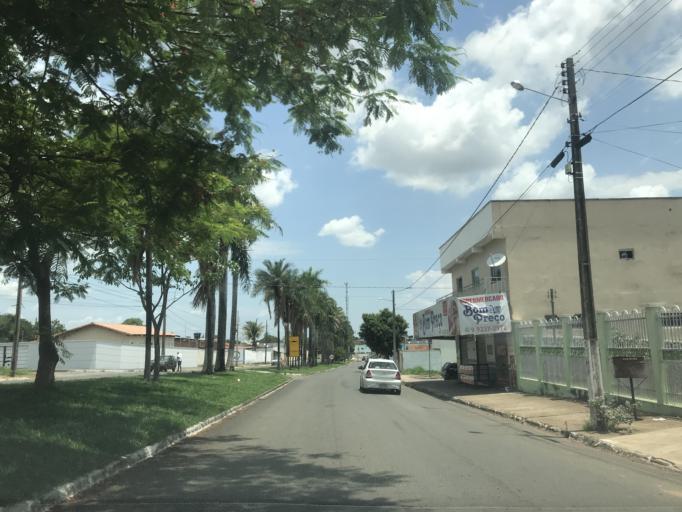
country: BR
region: Goias
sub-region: Bela Vista De Goias
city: Bela Vista de Goias
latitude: -17.0562
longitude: -48.6655
